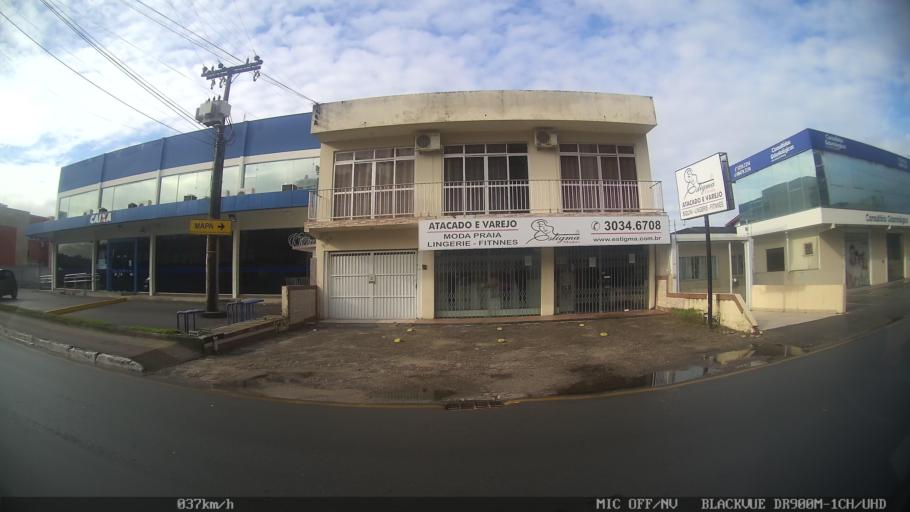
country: BR
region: Santa Catarina
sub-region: Sao Jose
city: Campinas
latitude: -27.6025
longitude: -48.6194
